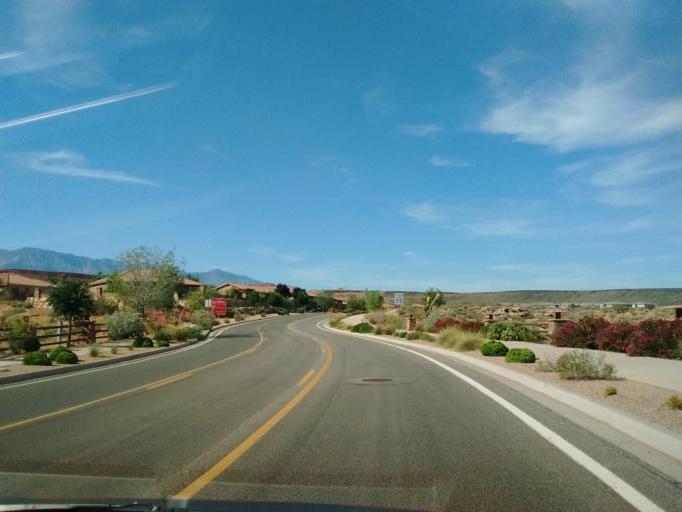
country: US
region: Utah
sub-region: Washington County
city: Washington
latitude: 37.1414
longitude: -113.4829
